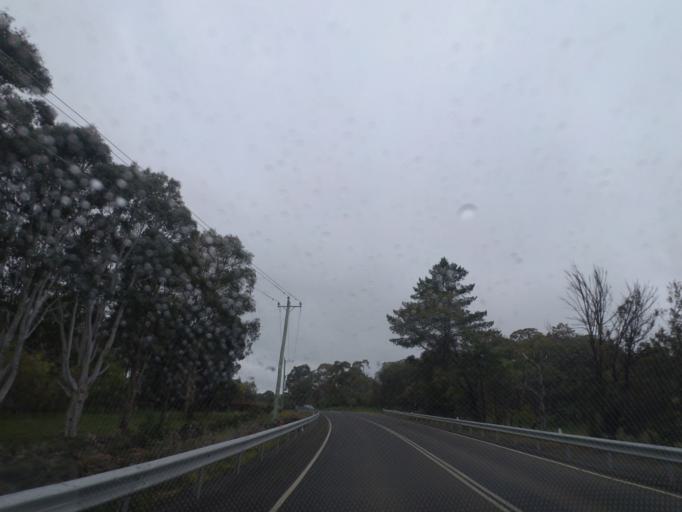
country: AU
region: Victoria
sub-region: Hume
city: Sunbury
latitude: -37.3526
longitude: 144.6385
